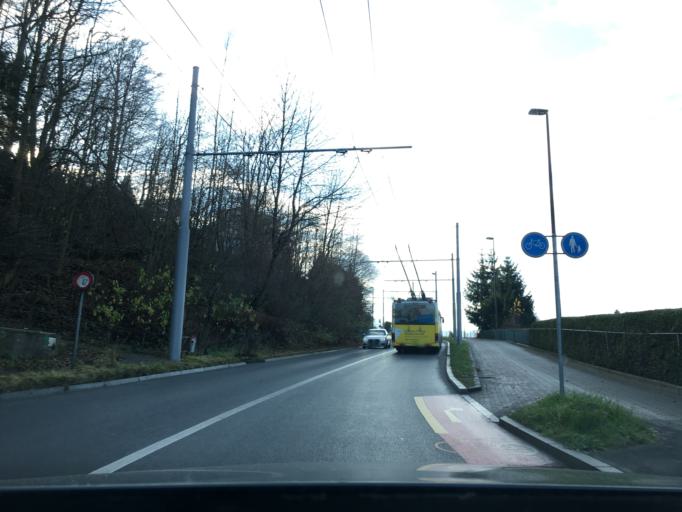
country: CH
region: Lucerne
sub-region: Lucerne-Land District
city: Adligenswil
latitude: 47.0530
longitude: 8.3447
